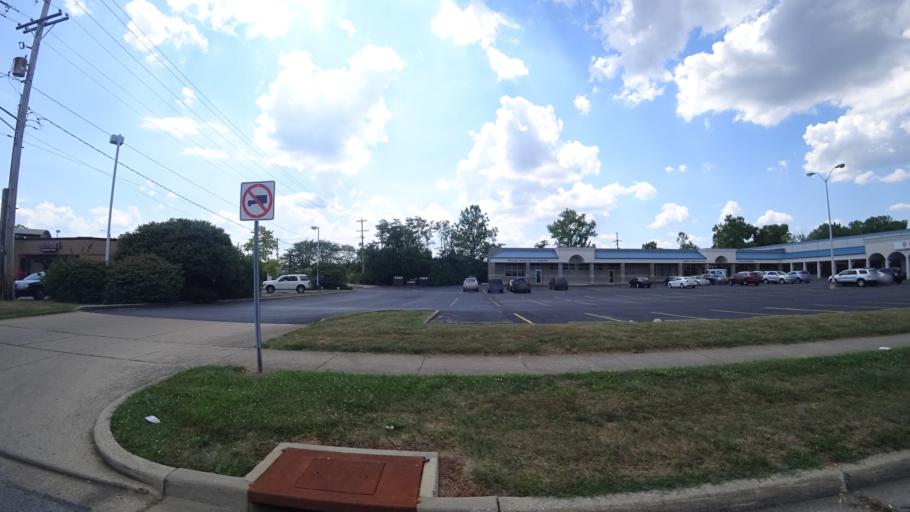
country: US
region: Ohio
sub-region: Butler County
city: Hamilton
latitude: 39.4249
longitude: -84.5854
